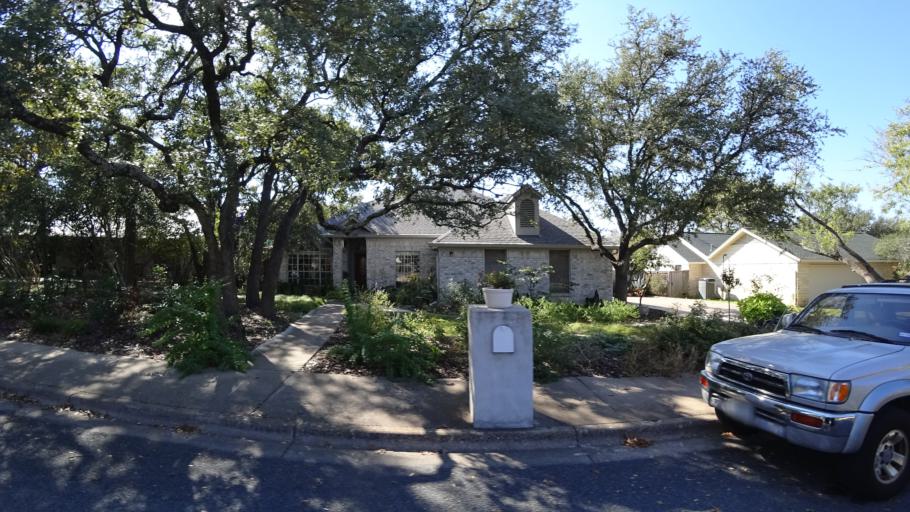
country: US
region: Texas
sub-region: Travis County
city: Barton Creek
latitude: 30.2303
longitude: -97.8735
